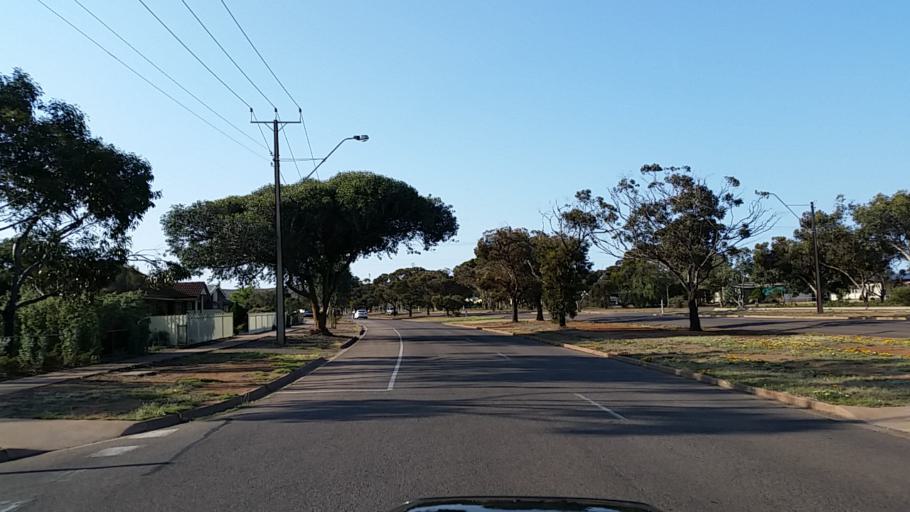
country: AU
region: South Australia
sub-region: Whyalla
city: Whyalla
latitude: -33.0237
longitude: 137.5314
